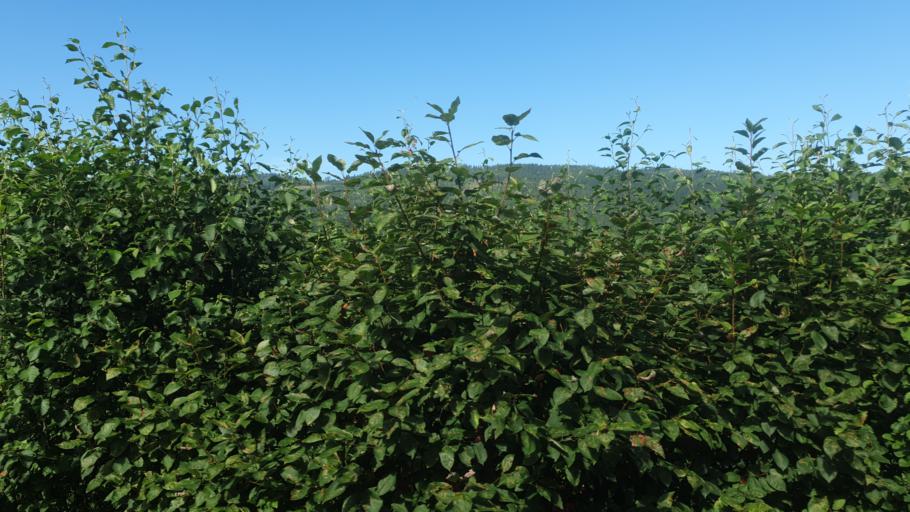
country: NO
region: Sor-Trondelag
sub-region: Orkdal
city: Orkanger
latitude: 63.2798
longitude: 9.8300
